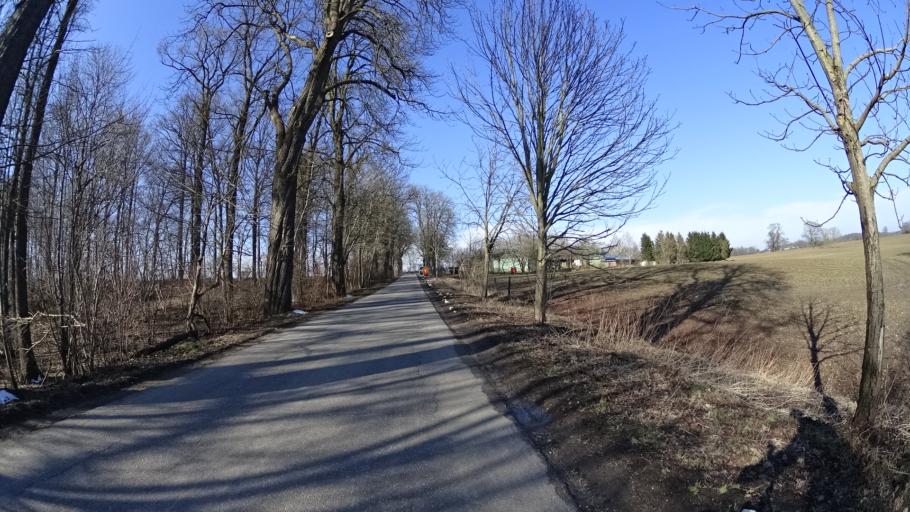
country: DE
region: Schleswig-Holstein
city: Schellhorn
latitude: 54.2516
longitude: 10.3238
